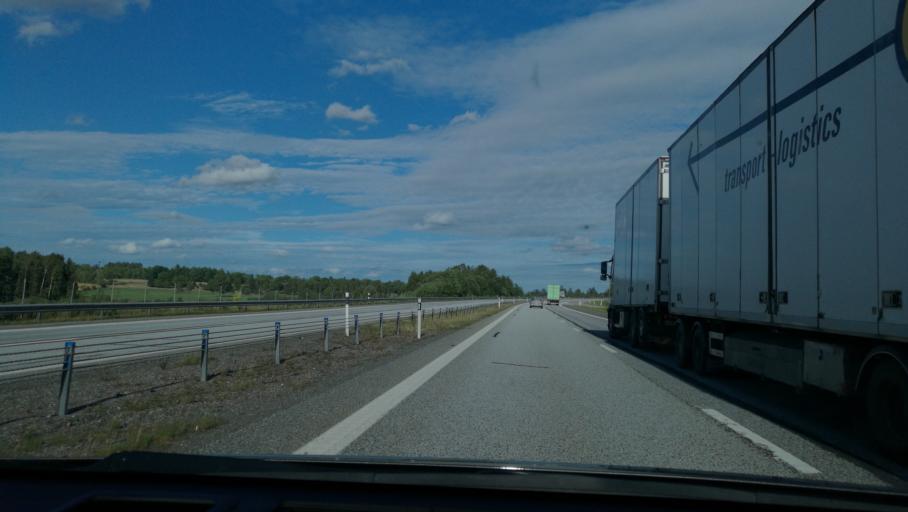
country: SE
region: OErebro
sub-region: Askersunds Kommun
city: Asbro
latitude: 59.0454
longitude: 14.9343
